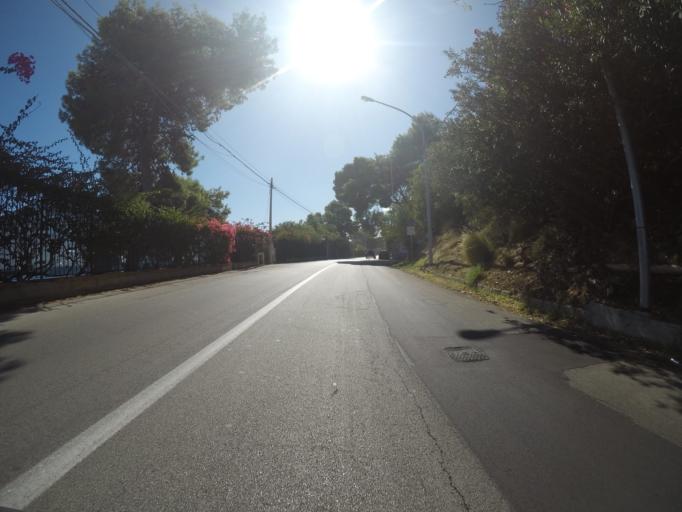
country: IT
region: Sicily
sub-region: Palermo
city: Palermo
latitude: 38.1835
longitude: 13.3641
